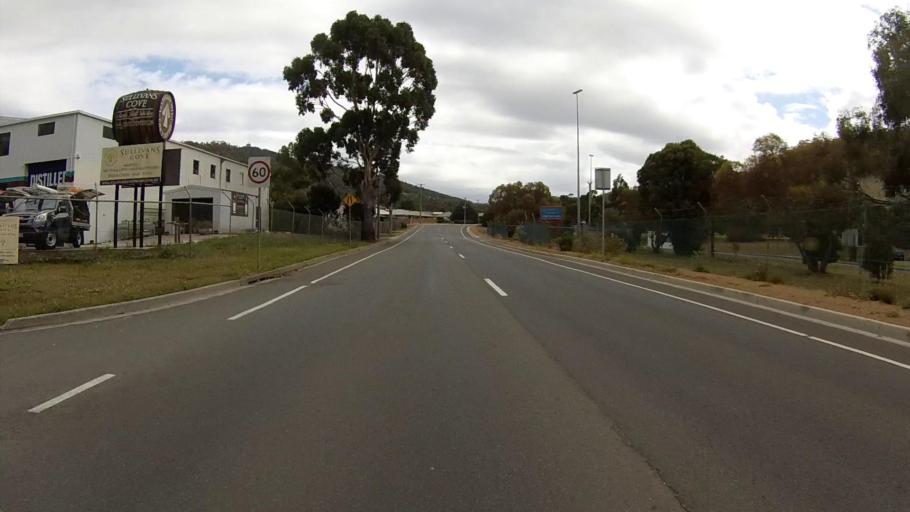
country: AU
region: Tasmania
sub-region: Clarence
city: Cambridge
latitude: -42.8355
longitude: 147.4475
